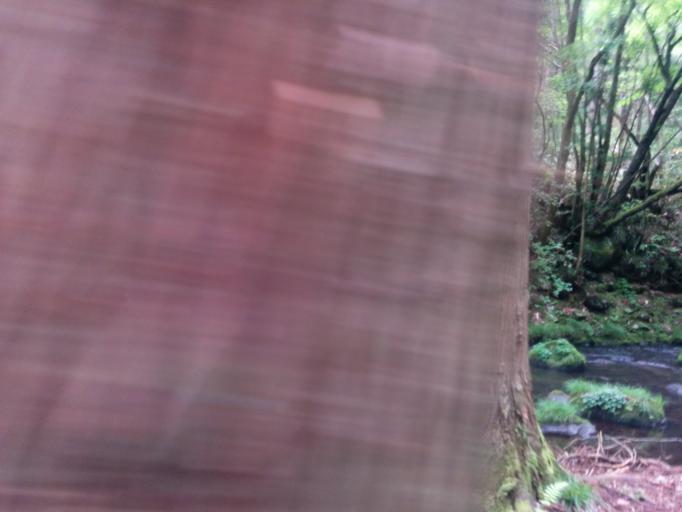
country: JP
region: Yamagata
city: Yuza
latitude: 39.1636
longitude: 139.9518
